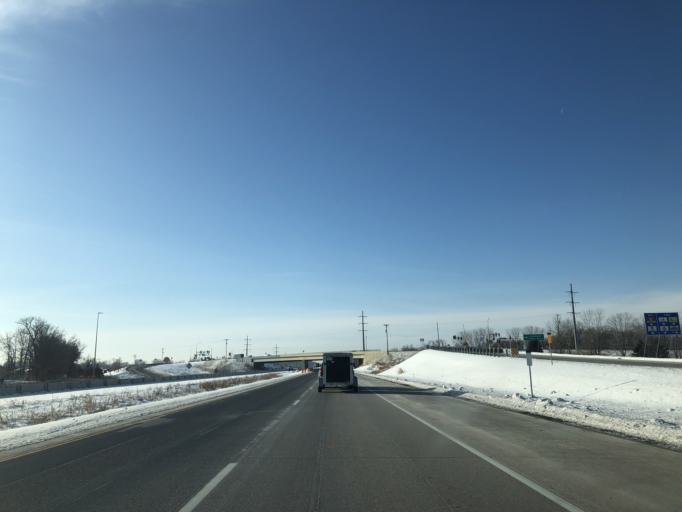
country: US
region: Minnesota
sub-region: Anoka County
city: Circle Pines
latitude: 45.1615
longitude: -93.1607
